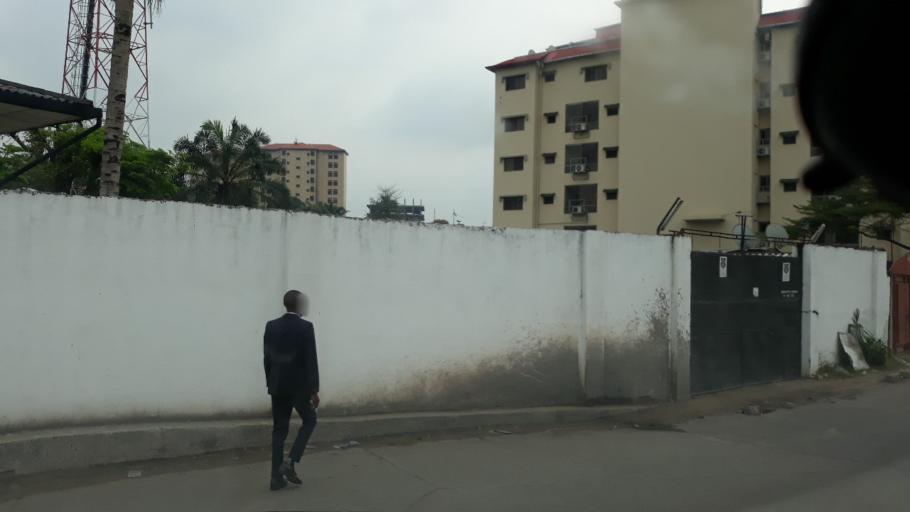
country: CD
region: Kinshasa
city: Kinshasa
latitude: -4.3196
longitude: 15.2786
